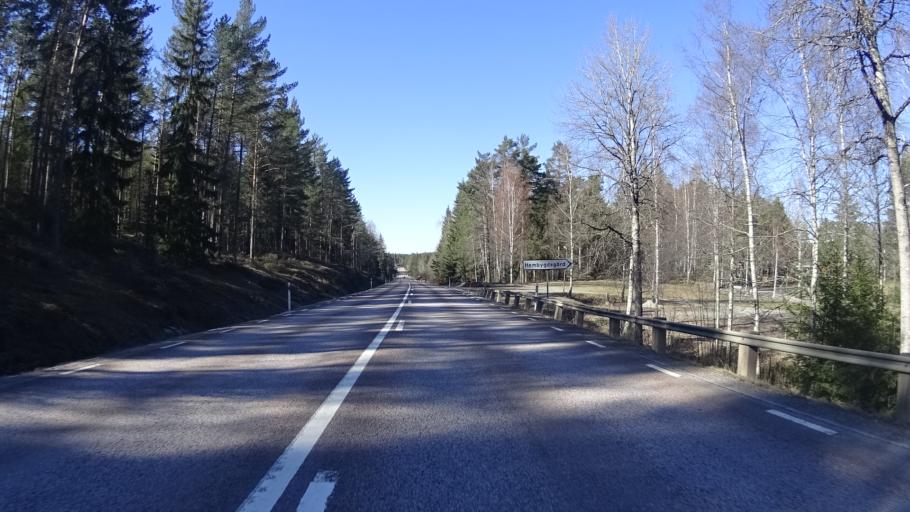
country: SE
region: Vaermland
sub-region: Karlstads Kommun
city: Edsvalla
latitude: 59.5959
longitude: 13.0065
